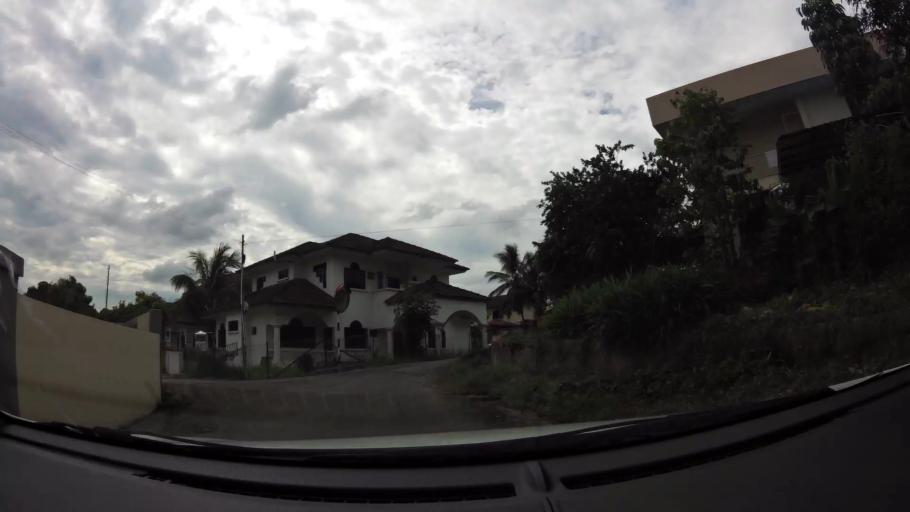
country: BN
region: Brunei and Muara
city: Bandar Seri Begawan
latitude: 4.8839
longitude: 114.8993
